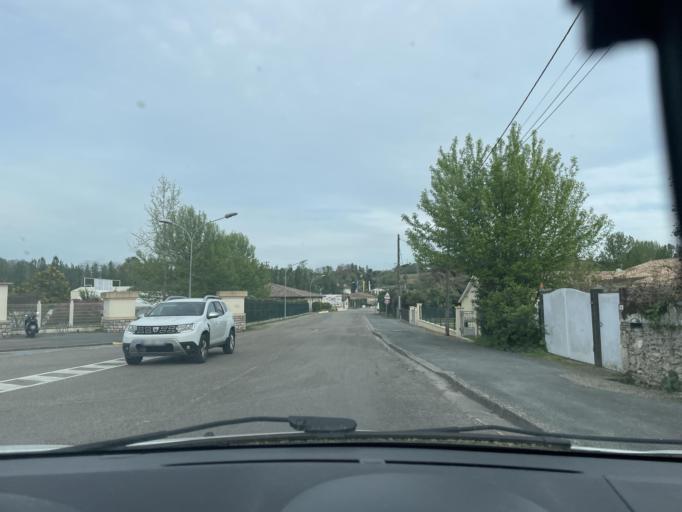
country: FR
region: Aquitaine
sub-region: Departement du Lot-et-Garonne
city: Casteljaloux
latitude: 44.3205
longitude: 0.0896
